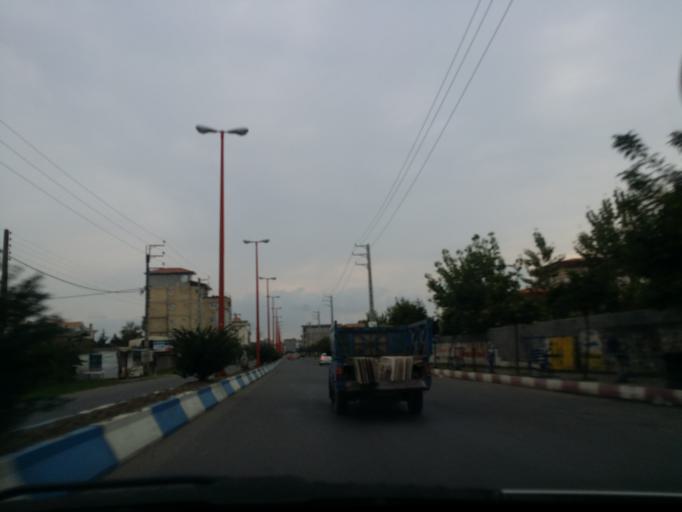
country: IR
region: Mazandaran
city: `Abbasabad
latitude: 36.7144
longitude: 51.1020
